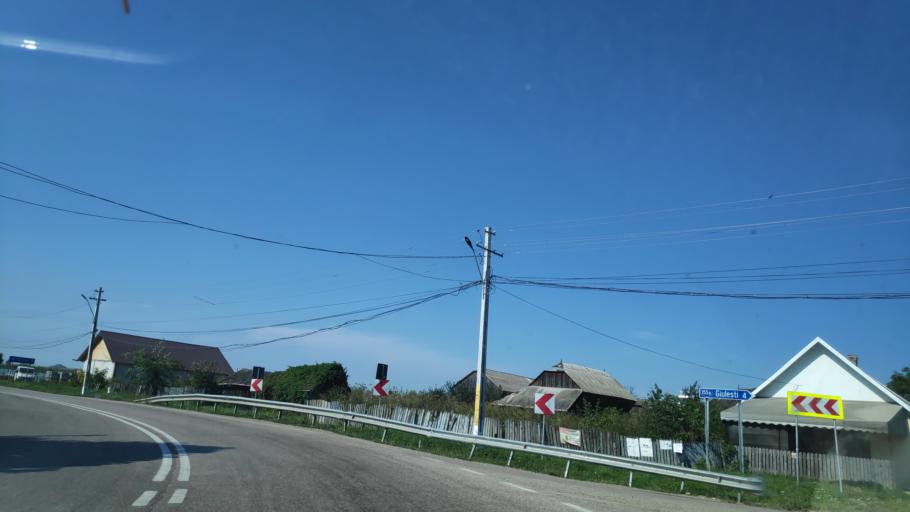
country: RO
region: Suceava
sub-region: Comuna Boroaia
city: Boroaia
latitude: 47.3579
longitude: 26.3443
